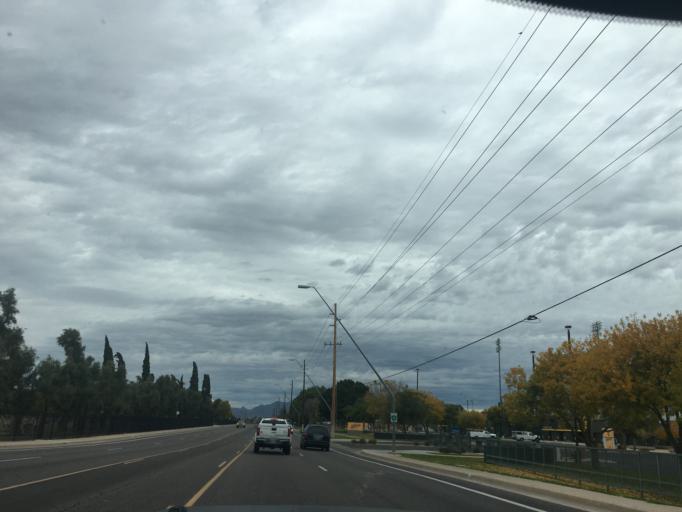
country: US
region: Arizona
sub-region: Maricopa County
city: Mesa
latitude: 33.4370
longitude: -111.8312
